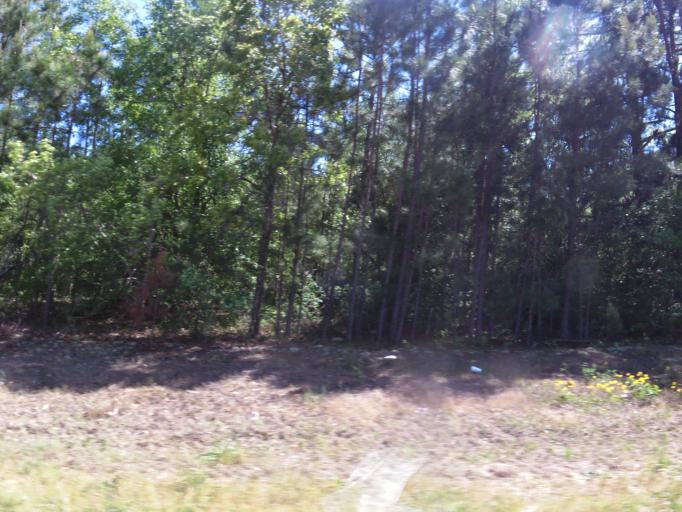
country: US
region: South Carolina
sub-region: Aiken County
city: New Ellenton
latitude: 33.5142
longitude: -81.5758
